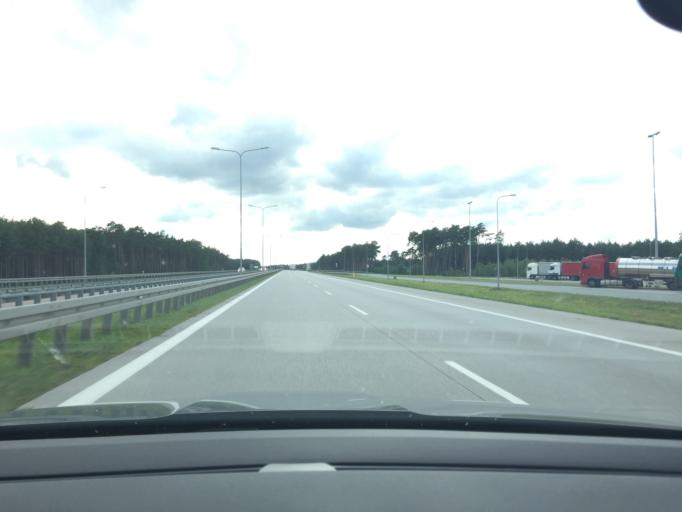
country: PL
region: Lubusz
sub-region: Powiat slubicki
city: Slubice
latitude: 52.3247
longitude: 14.6515
